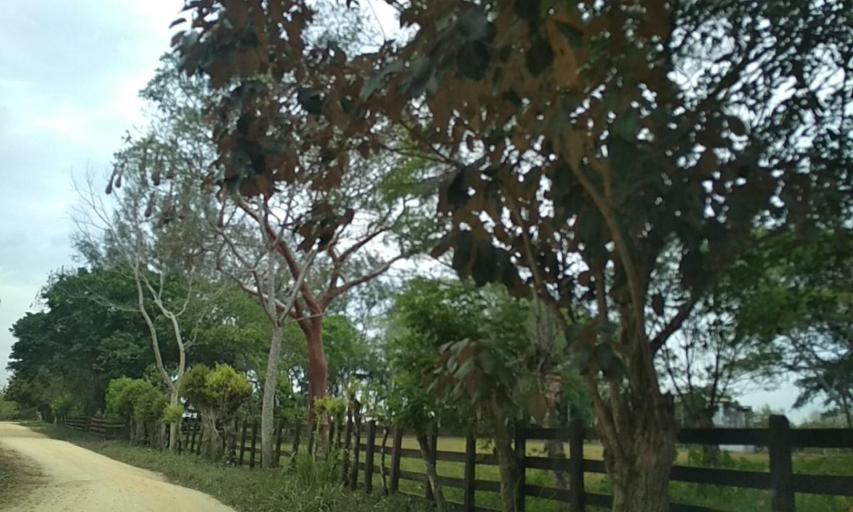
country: MX
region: Veracruz
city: Las Choapas
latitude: 17.8836
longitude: -94.1282
